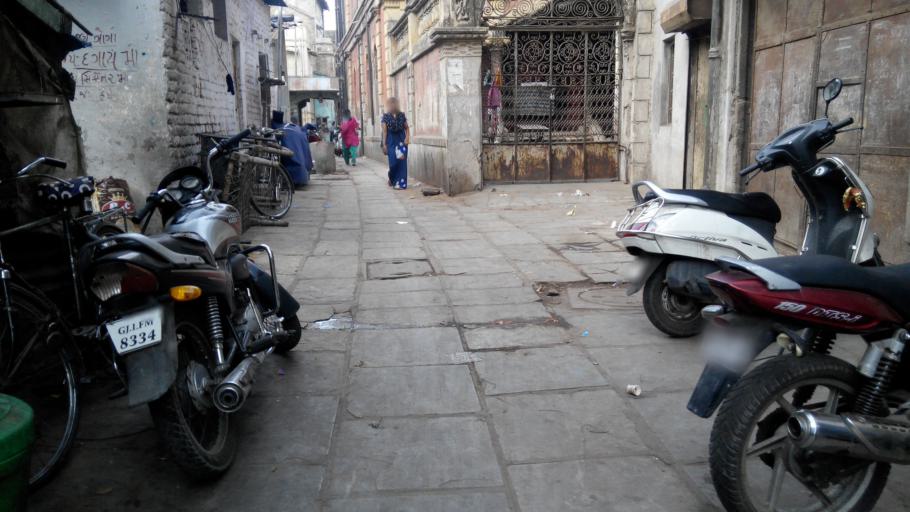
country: IN
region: Gujarat
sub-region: Ahmadabad
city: Ahmedabad
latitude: 23.0373
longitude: 72.5925
